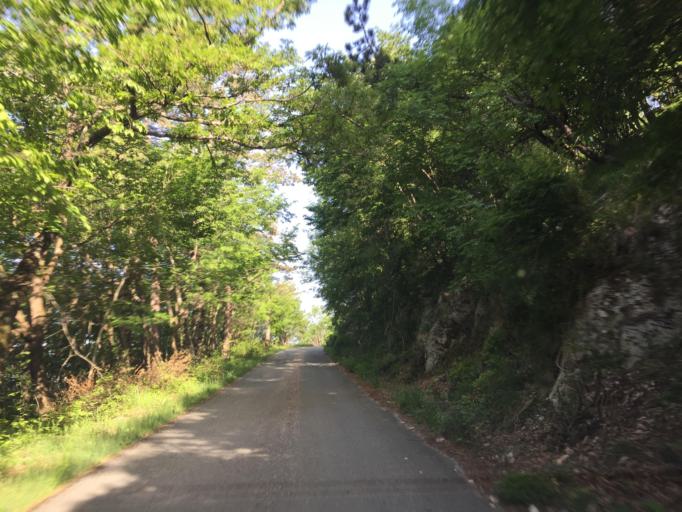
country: HR
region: Primorsko-Goranska
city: Klana
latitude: 45.4948
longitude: 14.4104
